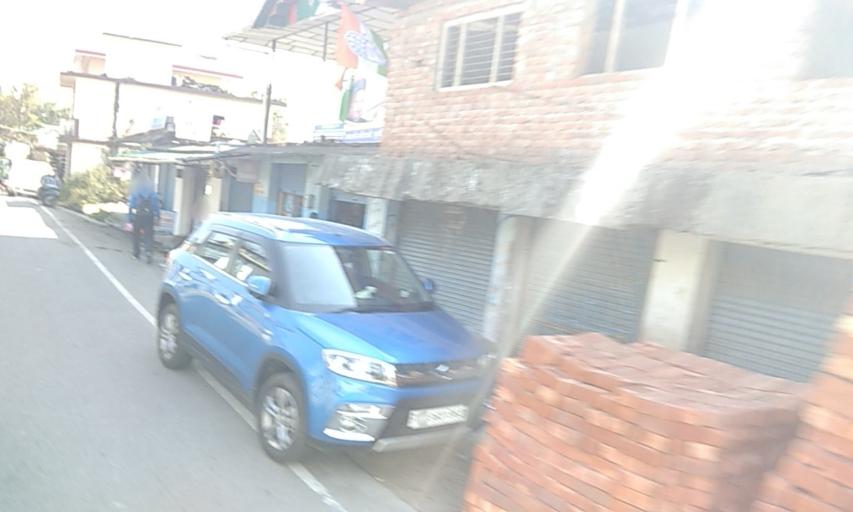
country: IN
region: Himachal Pradesh
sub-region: Kangra
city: Dharmsala
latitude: 32.1710
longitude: 76.3898
